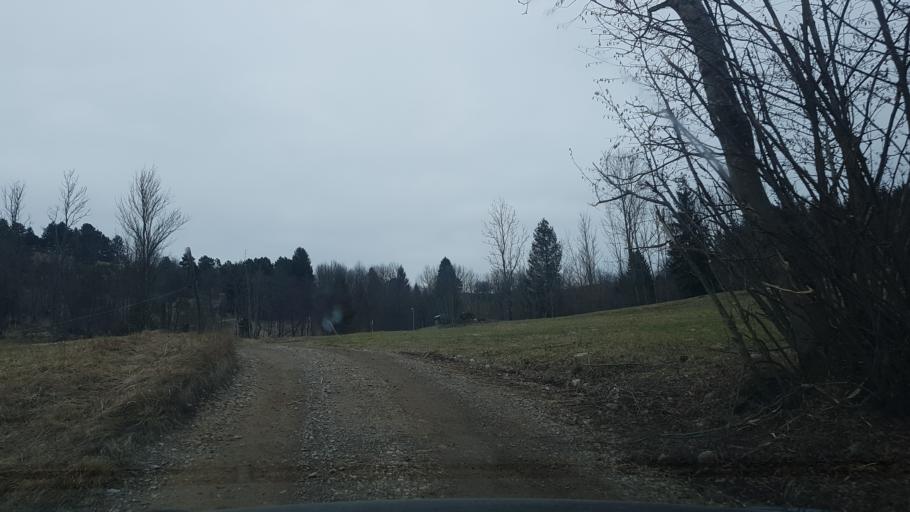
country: SI
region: Nova Gorica
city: Kromberk
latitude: 46.0227
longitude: 13.7008
